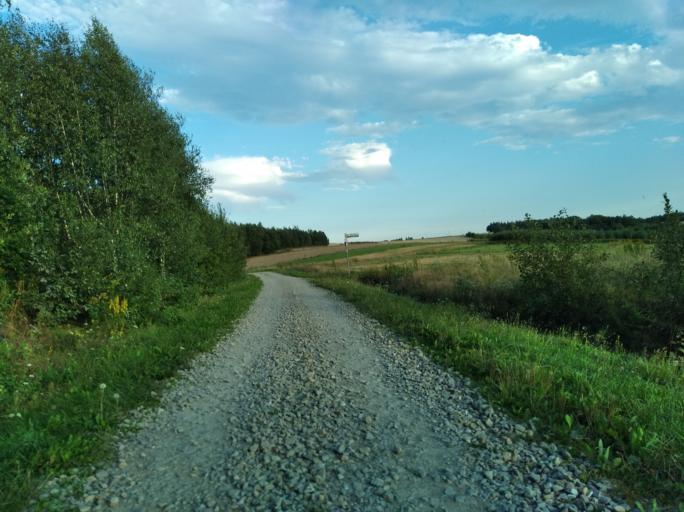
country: PL
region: Subcarpathian Voivodeship
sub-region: Powiat ropczycko-sedziszowski
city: Wielopole Skrzynskie
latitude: 49.9143
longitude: 21.5904
